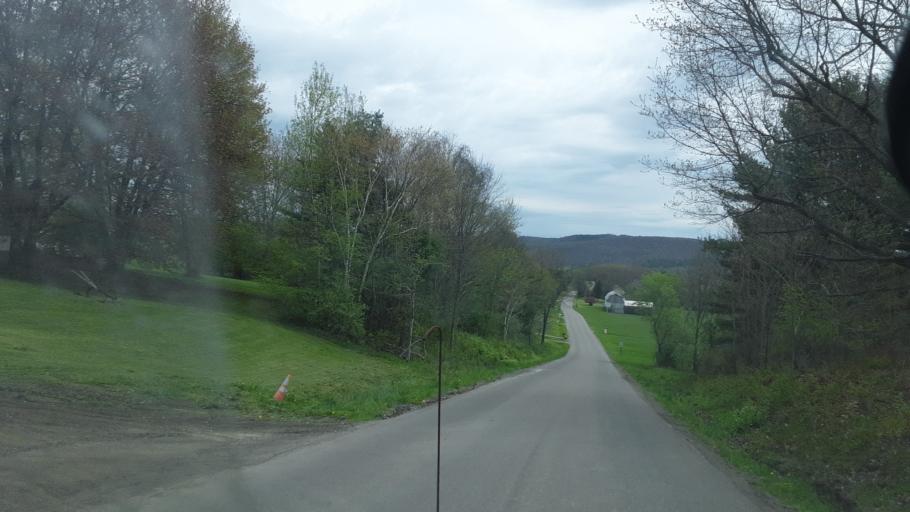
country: US
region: New York
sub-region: Steuben County
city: Addison
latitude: 42.0981
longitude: -77.2675
